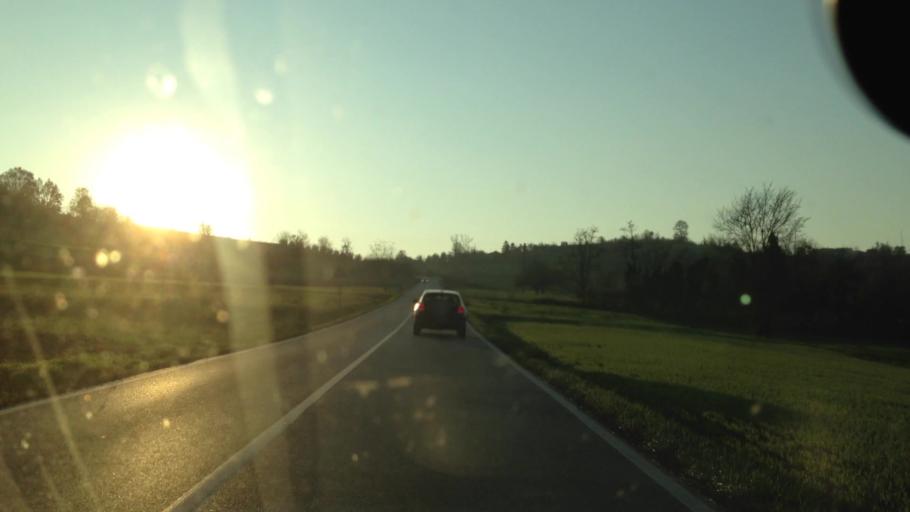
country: IT
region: Piedmont
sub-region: Provincia di Asti
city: Robella
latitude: 45.0867
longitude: 8.0943
